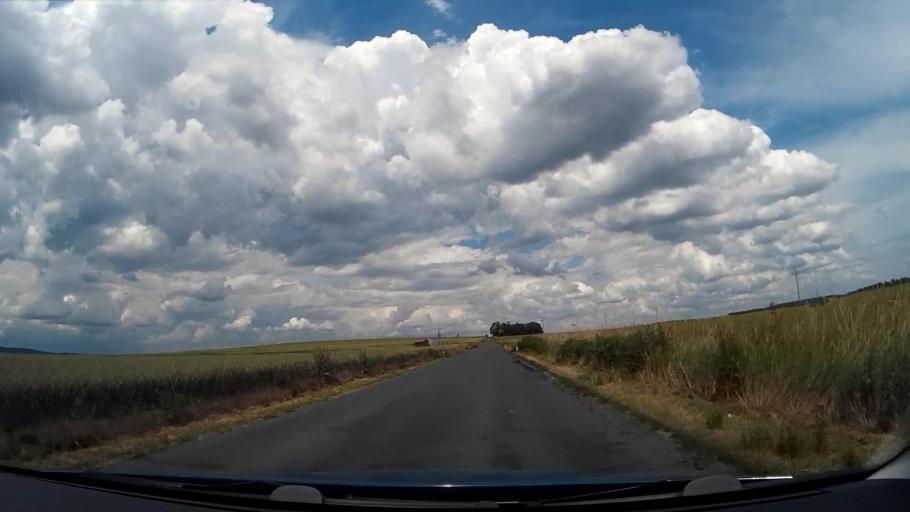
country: CZ
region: South Moravian
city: Orechov
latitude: 49.0938
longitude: 16.5266
